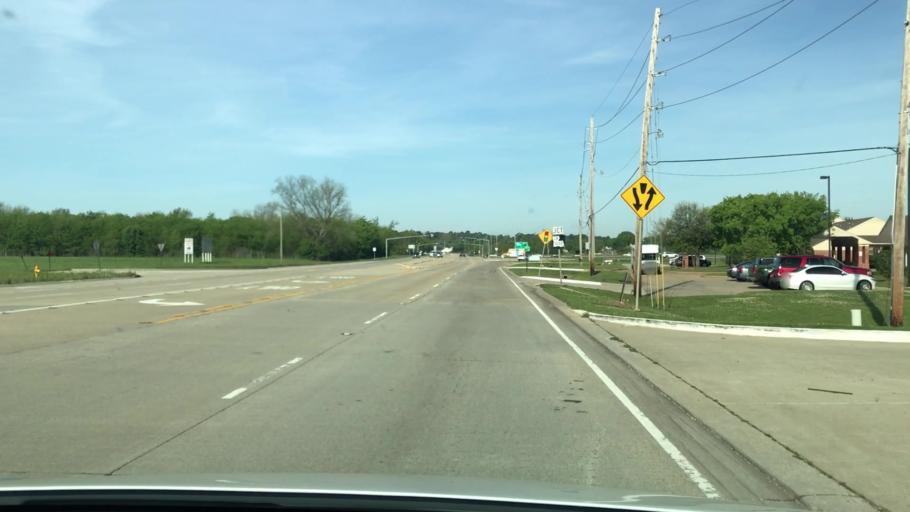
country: US
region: Louisiana
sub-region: Bossier Parish
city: Bossier City
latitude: 32.4010
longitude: -93.7111
